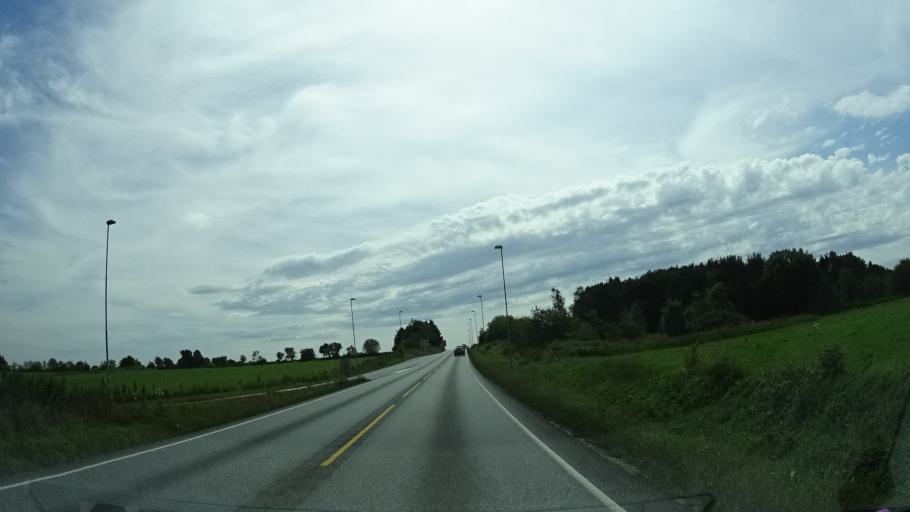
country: NO
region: Rogaland
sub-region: Randaberg
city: Randaberg
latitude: 59.0052
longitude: 5.6425
